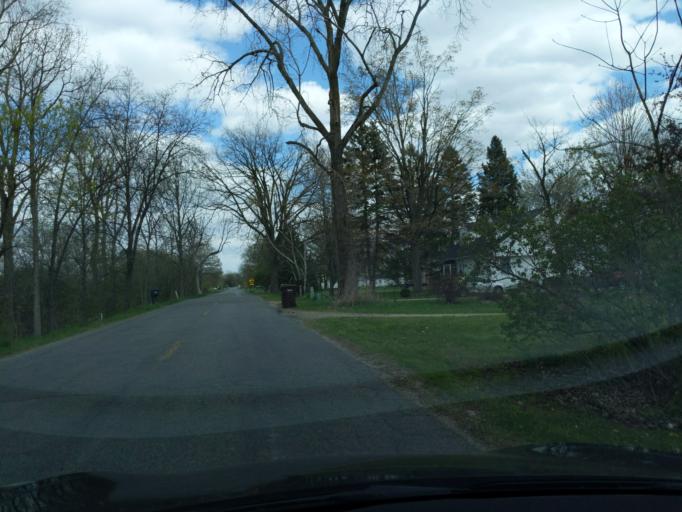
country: US
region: Michigan
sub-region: Ingham County
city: Holt
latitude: 42.6258
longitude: -84.5662
